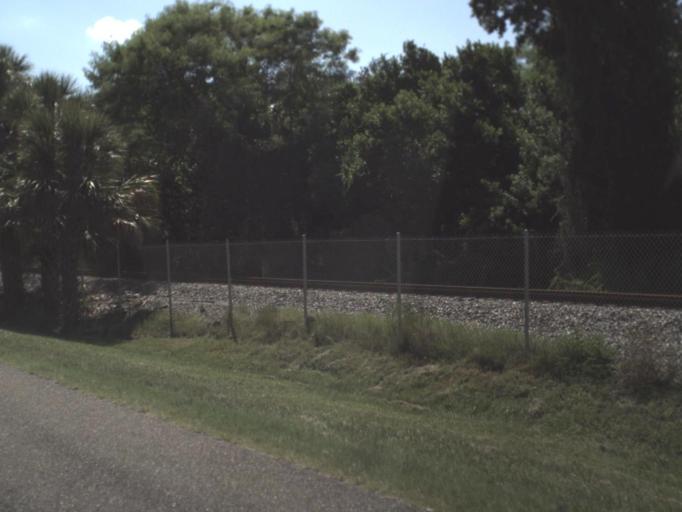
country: US
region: Florida
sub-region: Hillsborough County
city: Tampa
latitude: 27.9259
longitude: -82.4888
